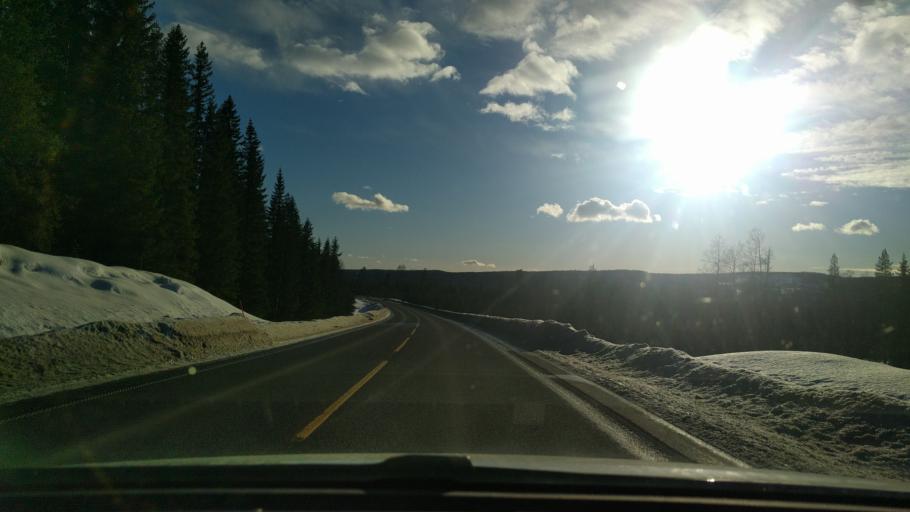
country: NO
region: Hedmark
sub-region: Trysil
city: Innbygda
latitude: 61.1030
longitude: 12.0096
